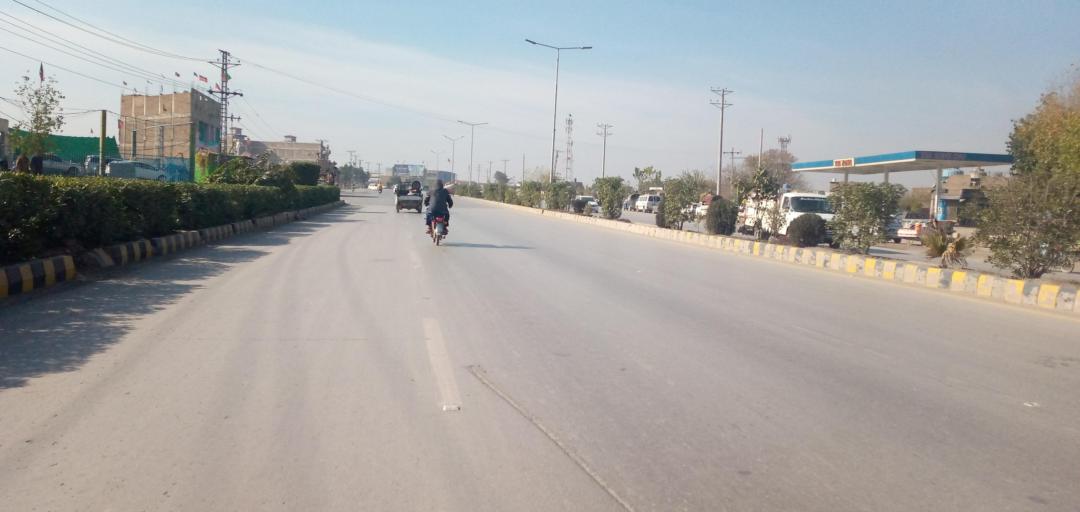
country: PK
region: Khyber Pakhtunkhwa
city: Peshawar
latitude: 33.9605
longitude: 71.5128
